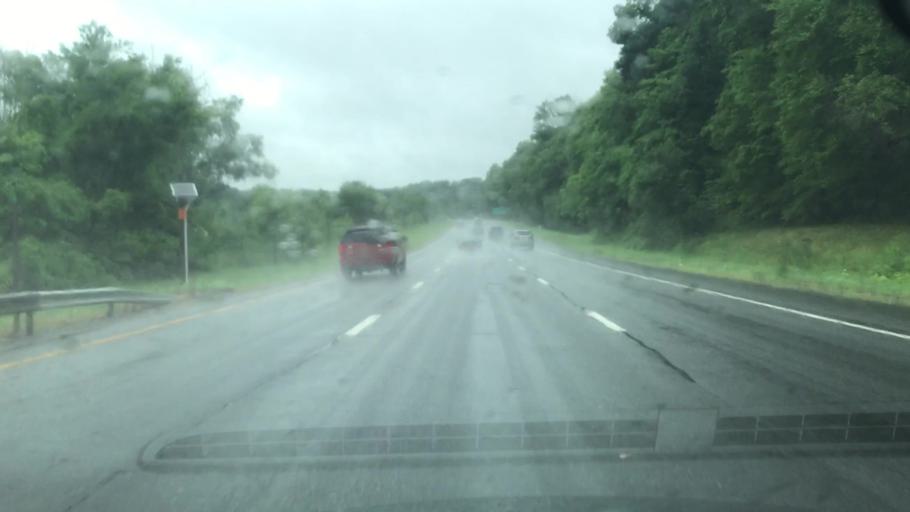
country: US
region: New York
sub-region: Westchester County
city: Yorktown Heights
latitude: 41.2481
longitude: -73.8122
